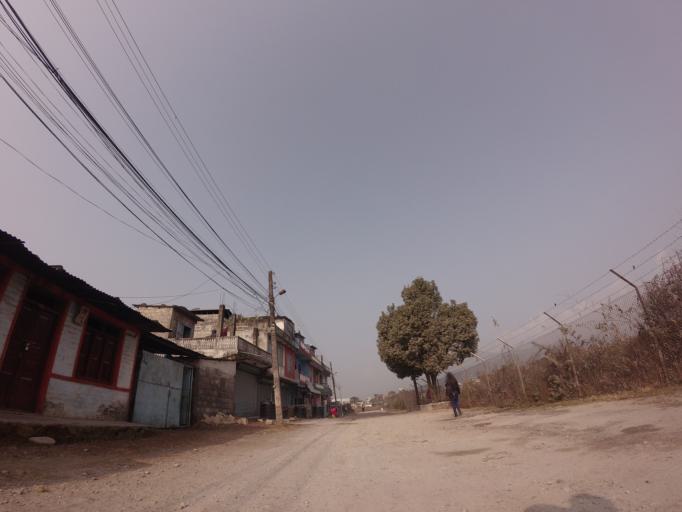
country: NP
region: Western Region
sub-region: Gandaki Zone
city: Pokhara
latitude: 28.1982
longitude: 83.9810
